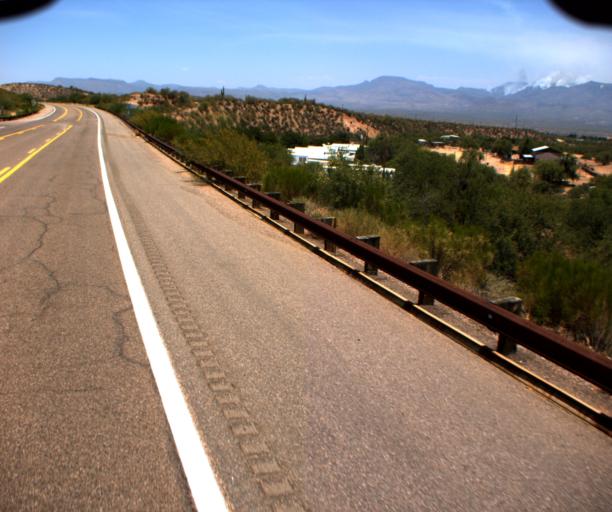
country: US
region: Arizona
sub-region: Gila County
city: Miami
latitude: 33.6043
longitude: -111.0086
